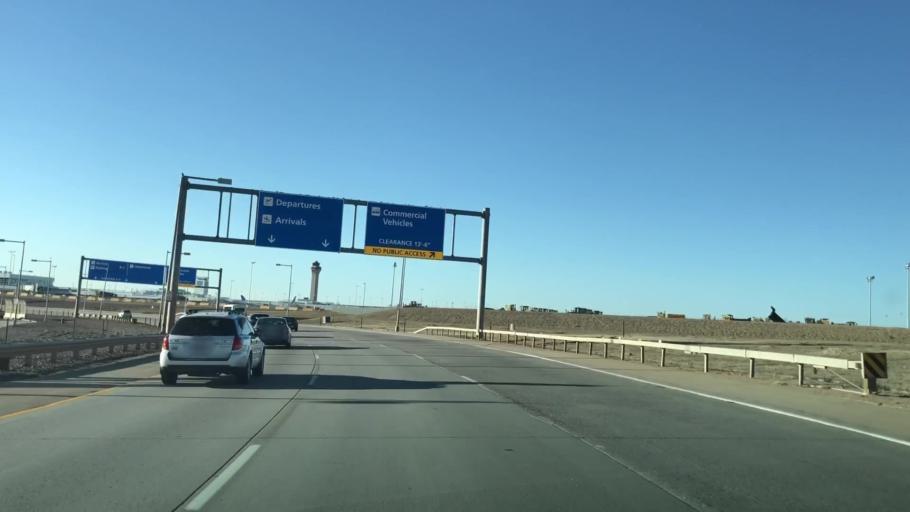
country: US
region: Colorado
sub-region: Weld County
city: Lochbuie
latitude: 39.8498
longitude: -104.6657
